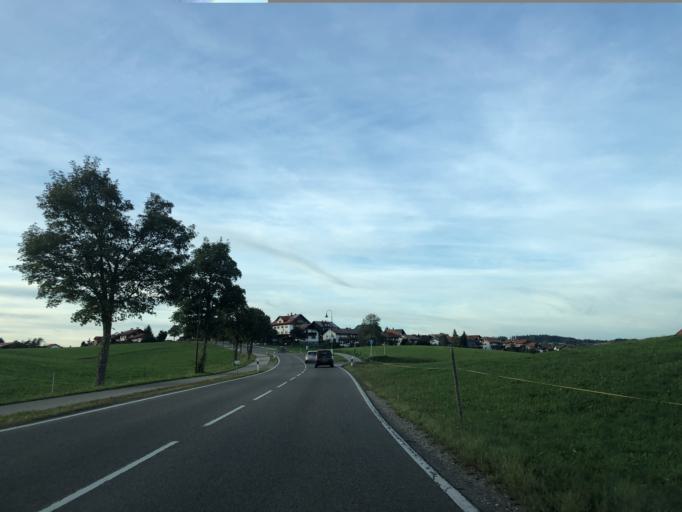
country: DE
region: Bavaria
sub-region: Swabia
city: Pfronten
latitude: 47.5903
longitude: 10.5574
